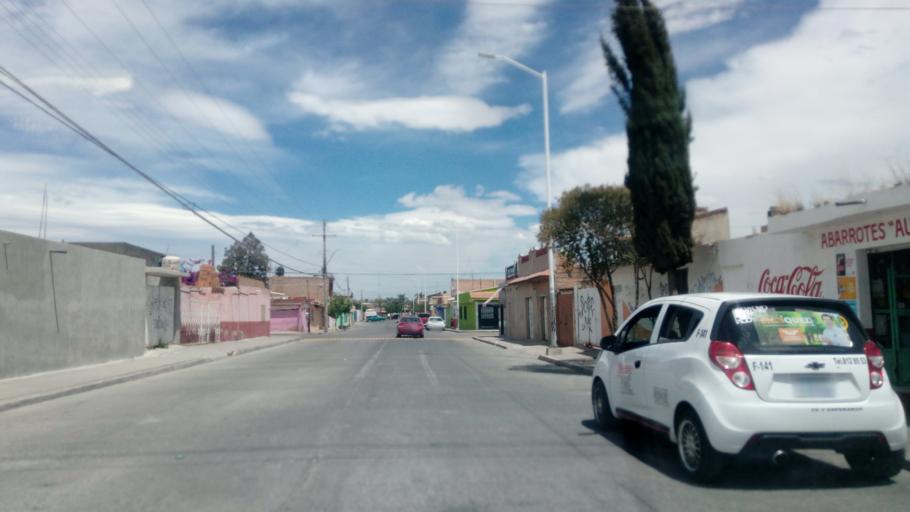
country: MX
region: Durango
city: Victoria de Durango
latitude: 23.9941
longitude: -104.6761
